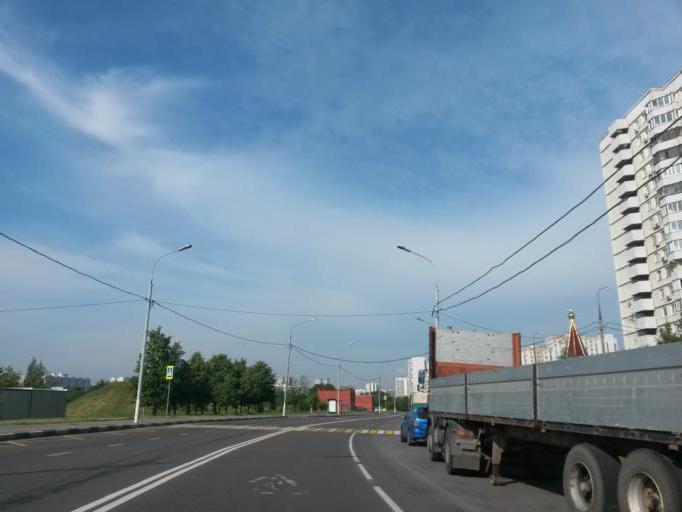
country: RU
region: Moscow
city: Brateyevo
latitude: 55.6318
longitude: 37.7699
